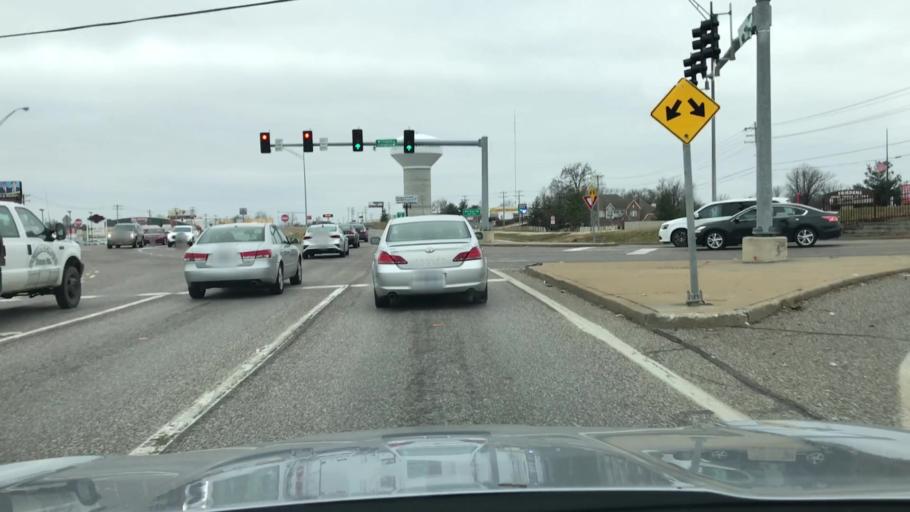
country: US
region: Missouri
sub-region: Saint Charles County
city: Saint Charles
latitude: 38.7690
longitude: -90.5237
